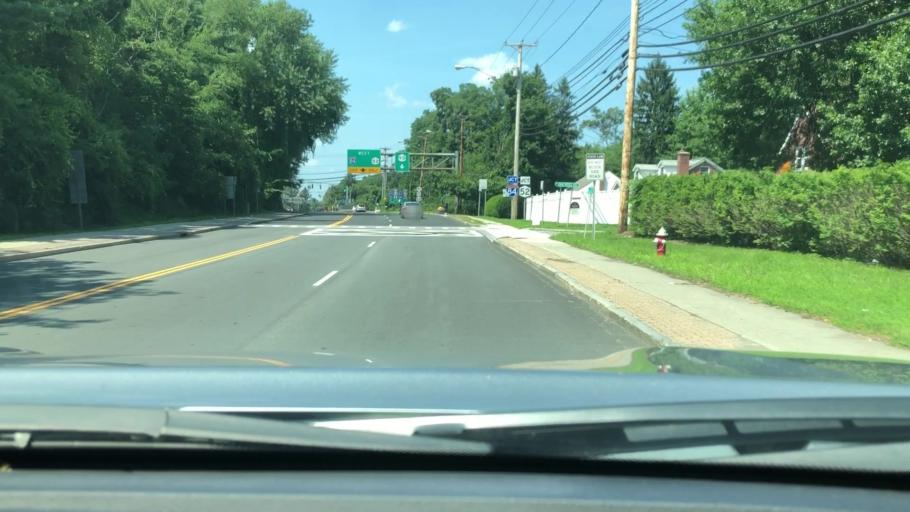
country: US
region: New York
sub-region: Dutchess County
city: Beacon
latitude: 41.5157
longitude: -73.9731
